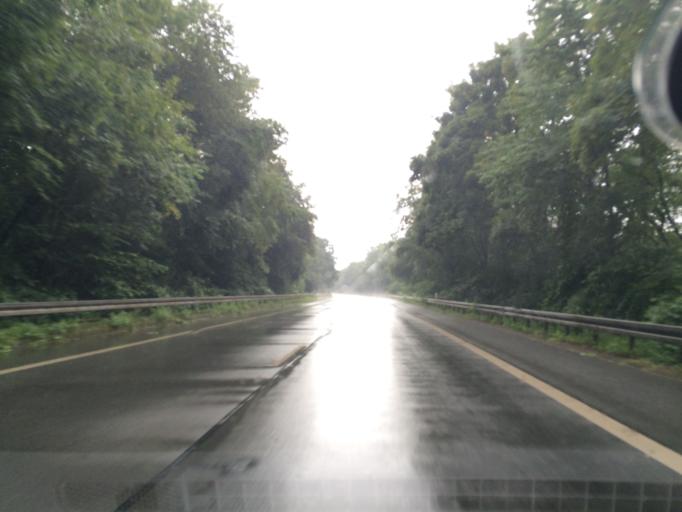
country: DE
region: North Rhine-Westphalia
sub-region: Regierungsbezirk Munster
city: Haltern
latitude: 51.7718
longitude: 7.2347
